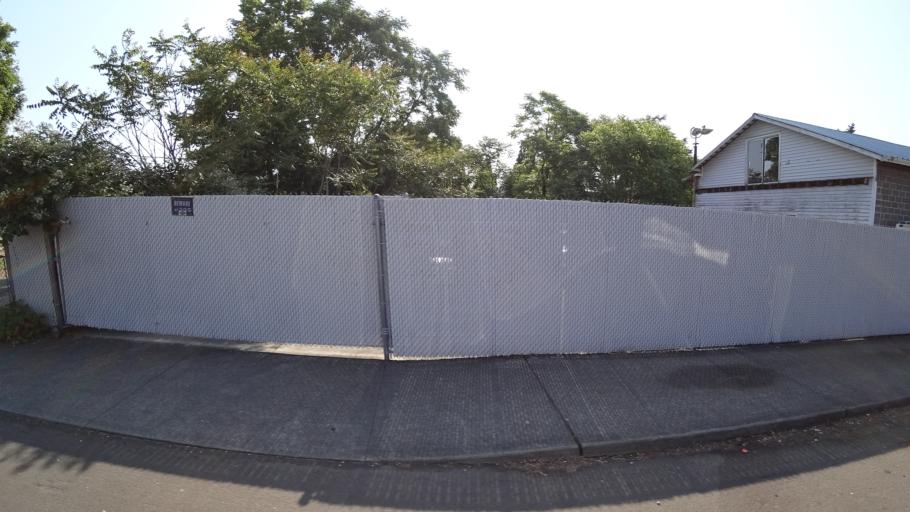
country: US
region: Oregon
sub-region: Multnomah County
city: Lents
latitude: 45.4617
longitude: -122.5945
